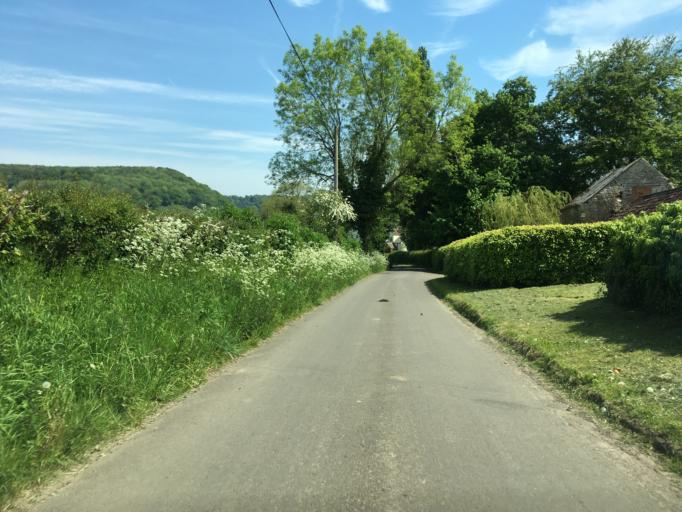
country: GB
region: England
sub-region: Gloucestershire
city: Dursley
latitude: 51.6631
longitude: -2.3607
